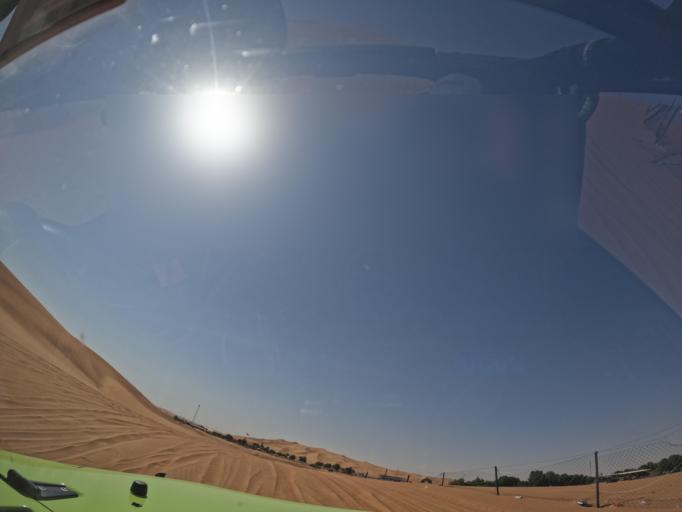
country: AE
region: Ash Shariqah
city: Adh Dhayd
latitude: 24.9576
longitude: 55.7166
